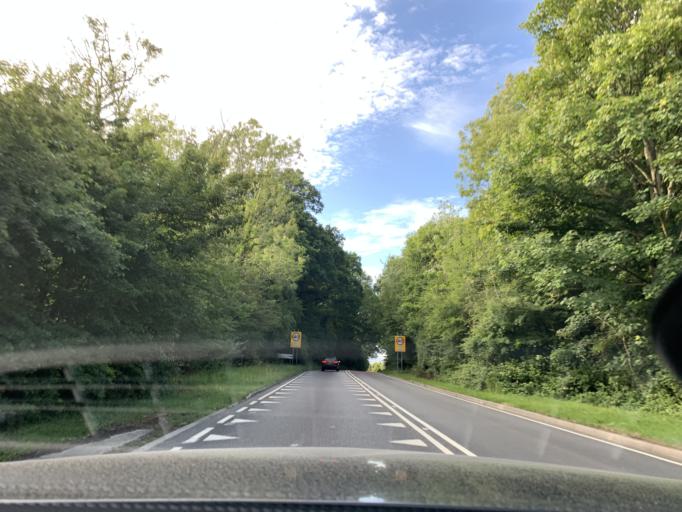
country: GB
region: England
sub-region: East Sussex
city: Robertsbridge
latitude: 51.0054
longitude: 0.4754
